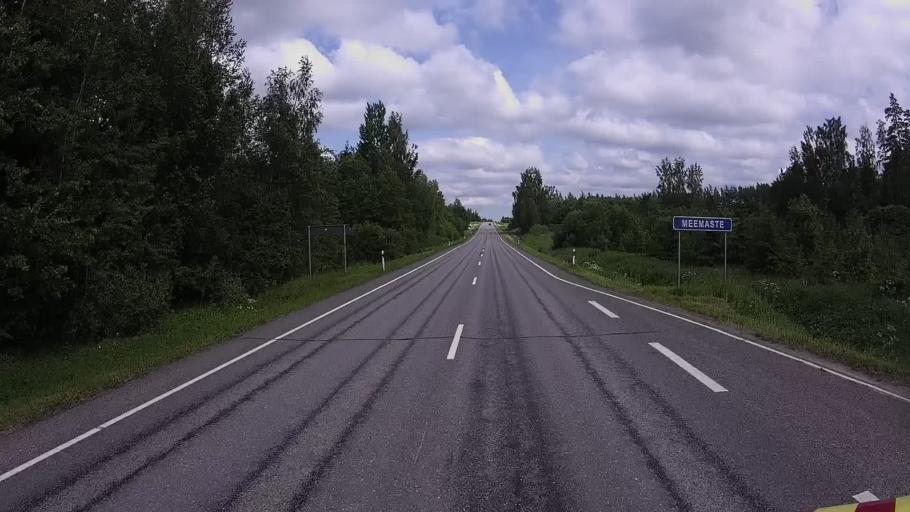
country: EE
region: Polvamaa
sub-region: Polva linn
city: Polva
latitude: 57.9995
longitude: 27.0594
